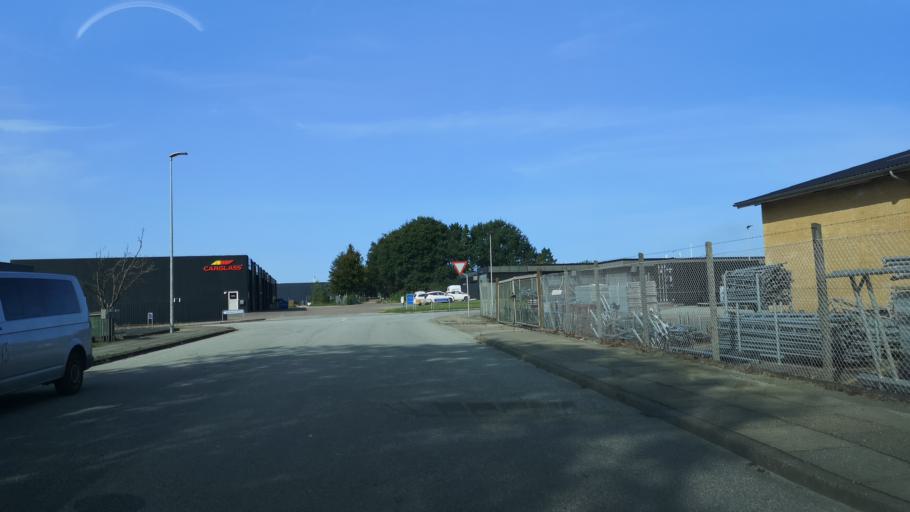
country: DK
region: Central Jutland
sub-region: Herning Kommune
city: Herning
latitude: 56.1538
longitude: 8.9803
